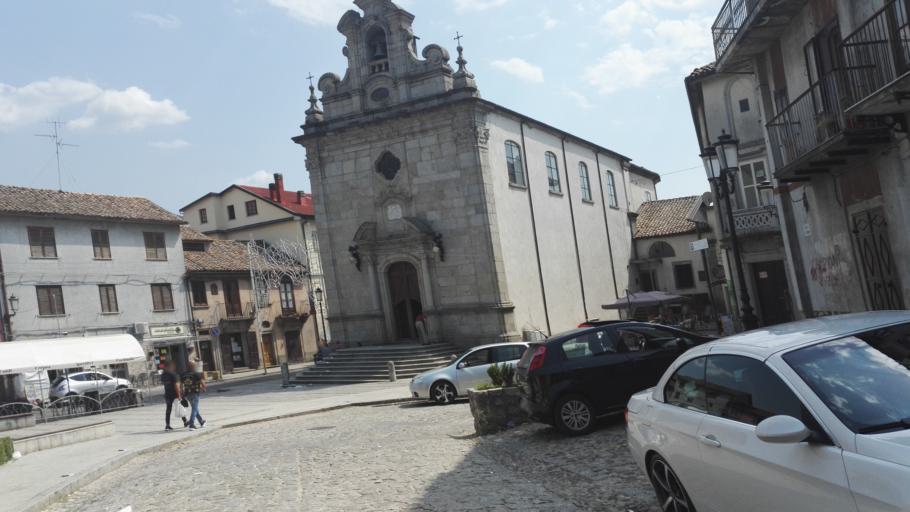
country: IT
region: Calabria
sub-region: Provincia di Vibo-Valentia
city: Serra San Bruno
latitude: 38.5783
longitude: 16.3306
